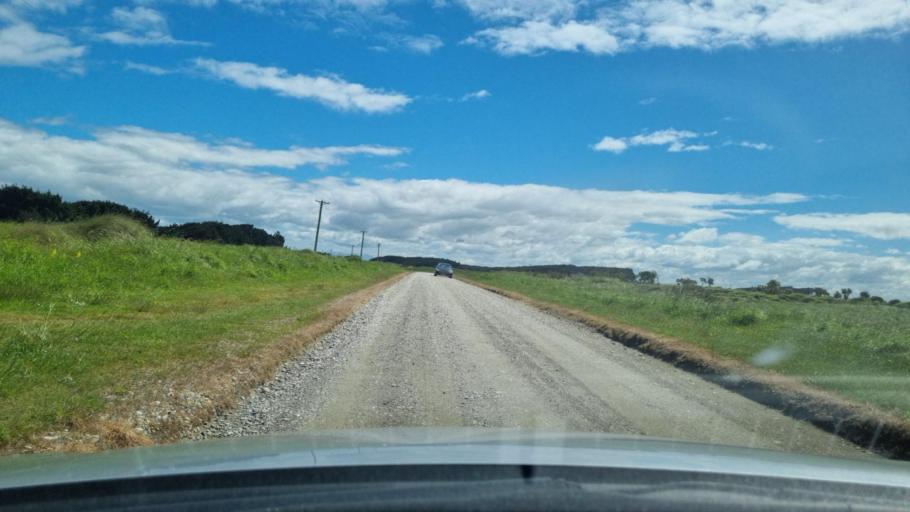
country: NZ
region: Southland
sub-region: Invercargill City
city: Invercargill
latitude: -46.4375
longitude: 168.2386
